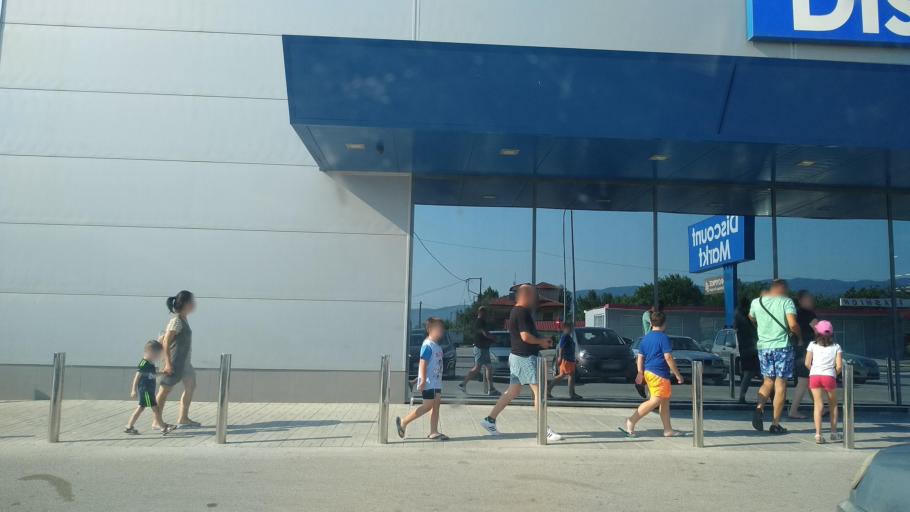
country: GR
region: Central Macedonia
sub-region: Nomos Thessalonikis
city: Stavros
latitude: 40.6662
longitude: 23.6864
